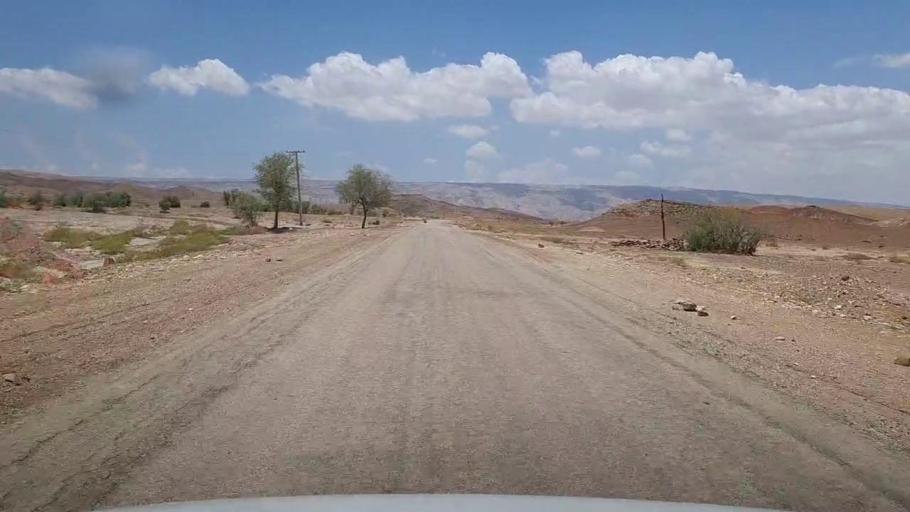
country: PK
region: Sindh
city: Bhan
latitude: 26.3171
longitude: 67.5705
